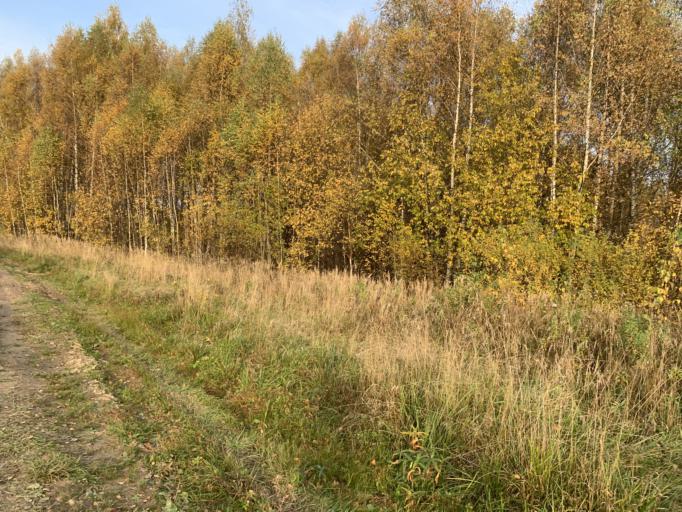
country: RU
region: Jaroslavl
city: Porech'ye-Rybnoye
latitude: 56.9844
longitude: 39.3850
